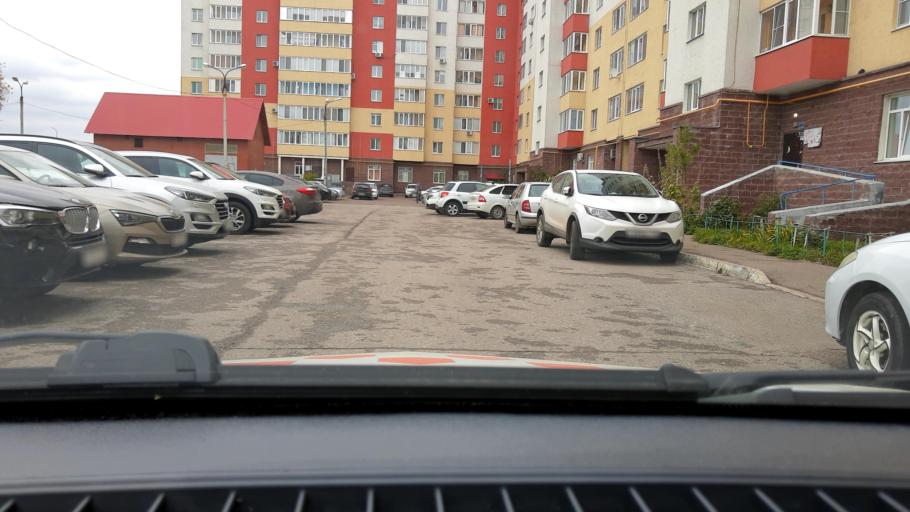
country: RU
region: Bashkortostan
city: Mikhaylovka
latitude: 54.7128
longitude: 55.8327
